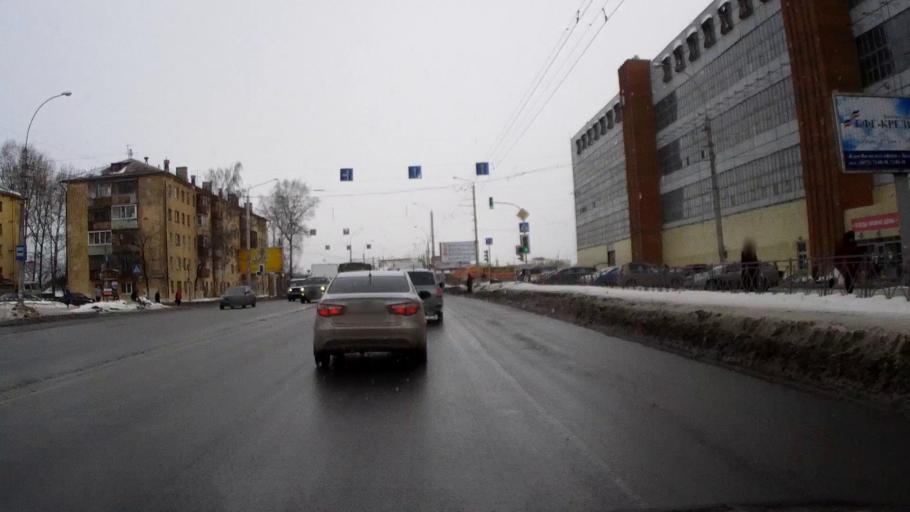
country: RU
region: Vologda
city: Vologda
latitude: 59.2132
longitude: 39.8550
